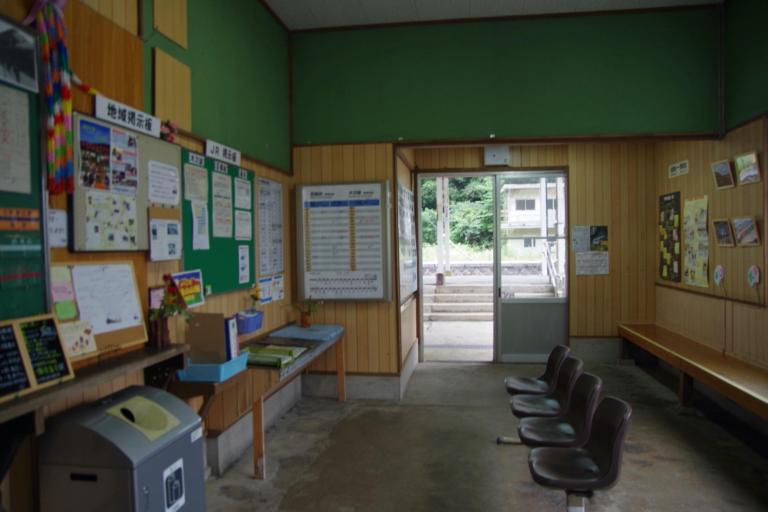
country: JP
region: Hiroshima
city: Shobara
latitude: 35.0012
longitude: 133.1479
